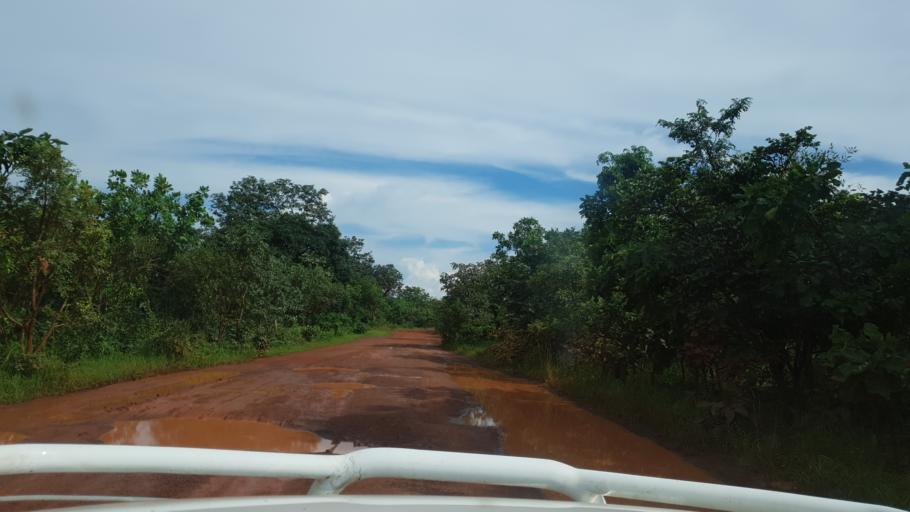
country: ML
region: Sikasso
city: Kolondieba
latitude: 10.7435
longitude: -6.9114
